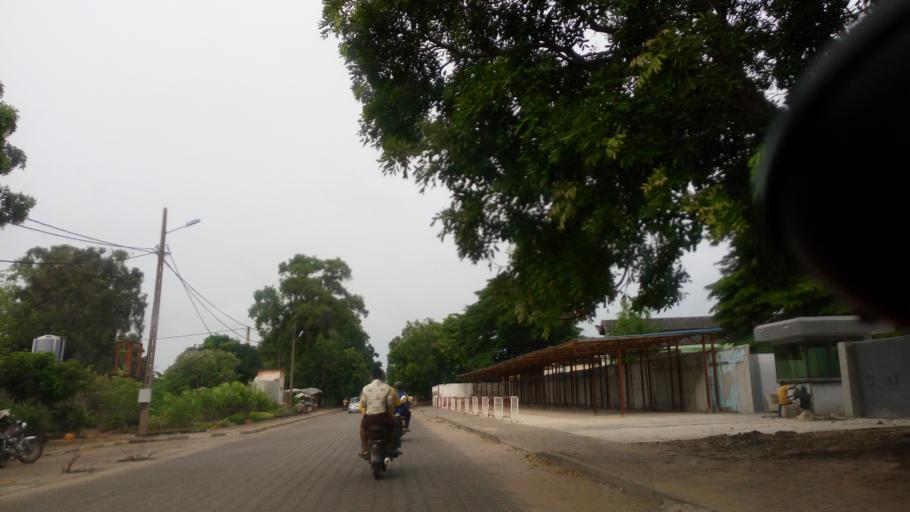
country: BJ
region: Littoral
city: Cotonou
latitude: 6.3565
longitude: 2.4097
